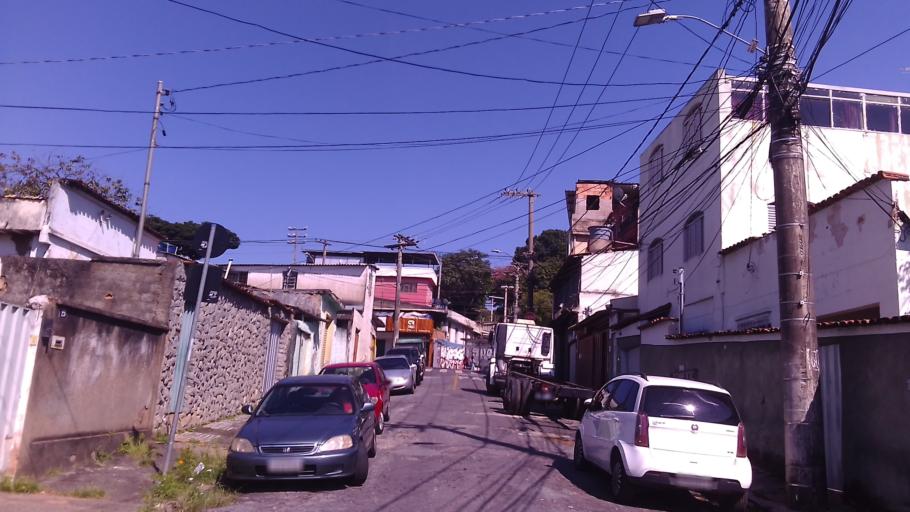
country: BR
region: Minas Gerais
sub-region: Belo Horizonte
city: Belo Horizonte
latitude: -19.8983
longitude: -43.9111
